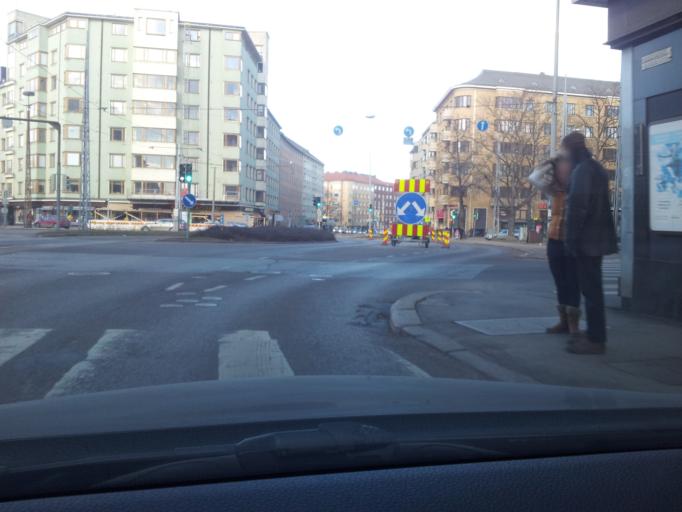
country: FI
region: Uusimaa
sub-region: Helsinki
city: Helsinki
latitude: 60.1786
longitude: 24.9228
